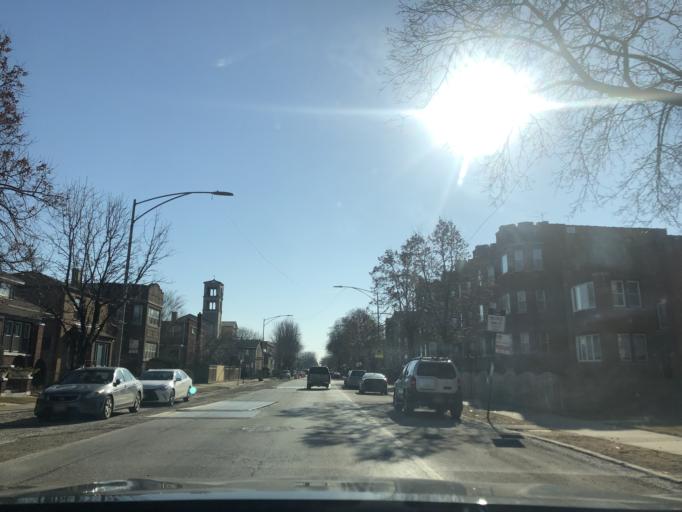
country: US
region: Indiana
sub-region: Lake County
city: Whiting
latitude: 41.7544
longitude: -87.5761
